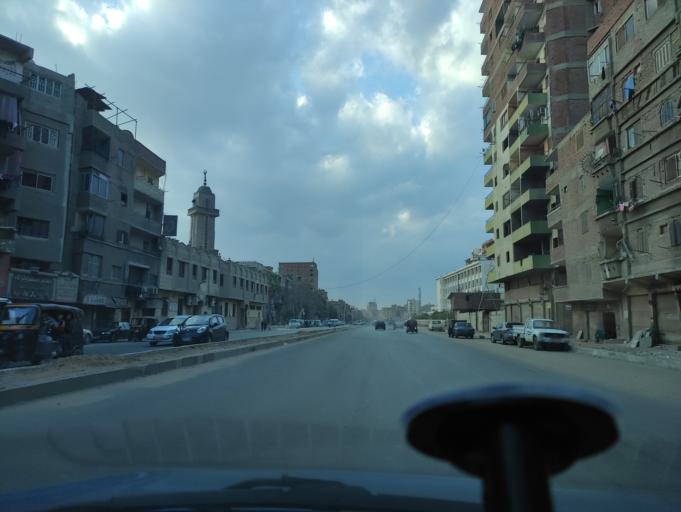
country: EG
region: Muhafazat al Qalyubiyah
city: Al Khankah
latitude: 30.1329
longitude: 31.3593
